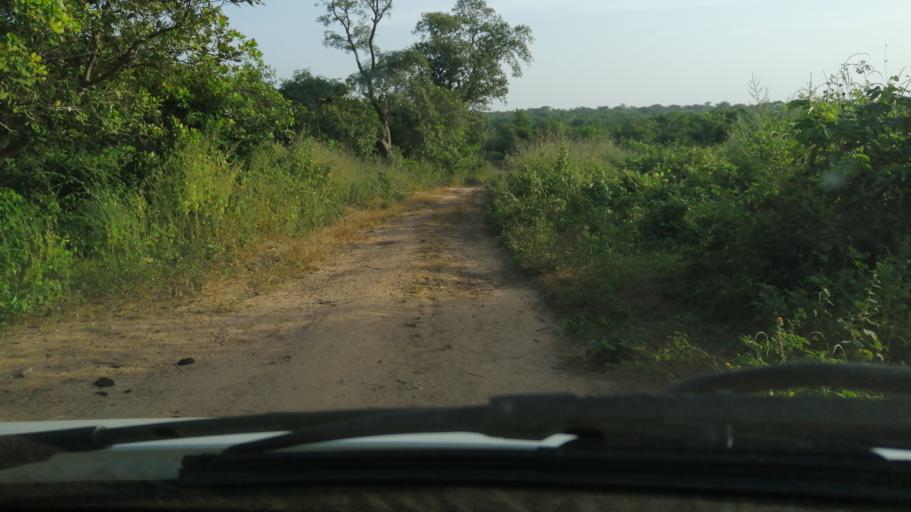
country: GW
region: Oio
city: Mansoa
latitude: 11.9918
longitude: -15.4698
